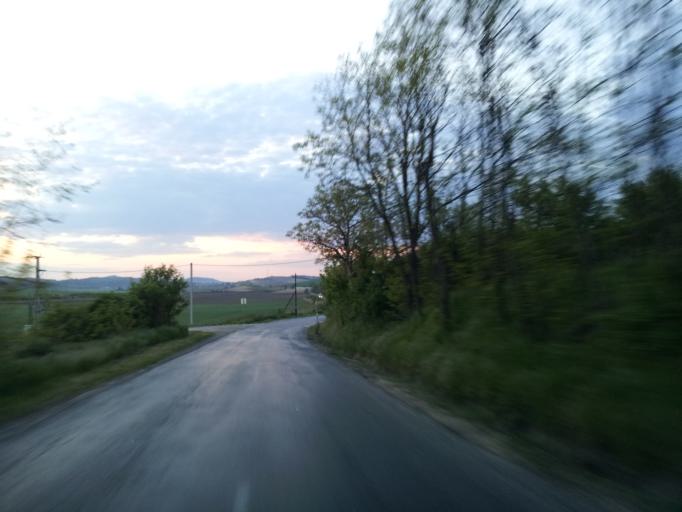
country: HU
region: Komarom-Esztergom
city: Csolnok
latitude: 47.6440
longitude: 18.7216
